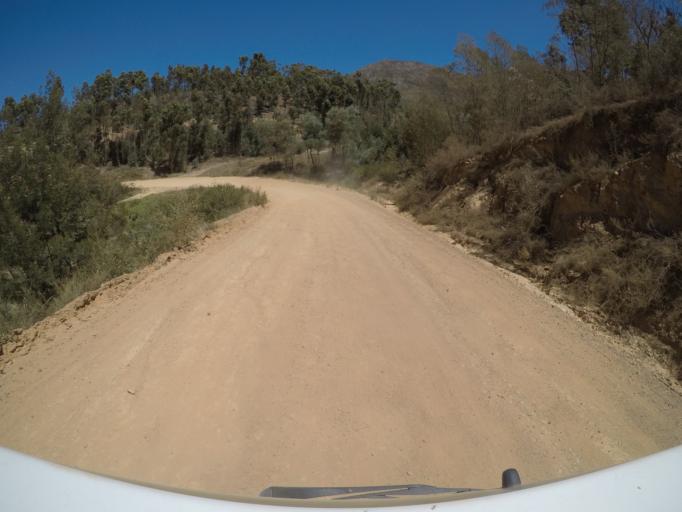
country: ZA
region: Western Cape
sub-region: Overberg District Municipality
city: Grabouw
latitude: -34.2070
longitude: 19.2136
